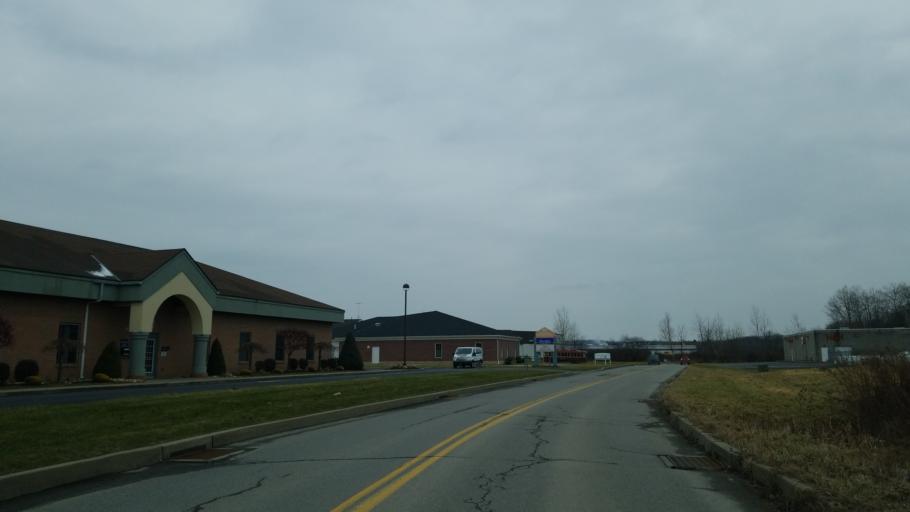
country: US
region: Pennsylvania
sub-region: Clearfield County
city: DuBois
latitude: 41.1207
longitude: -78.7518
